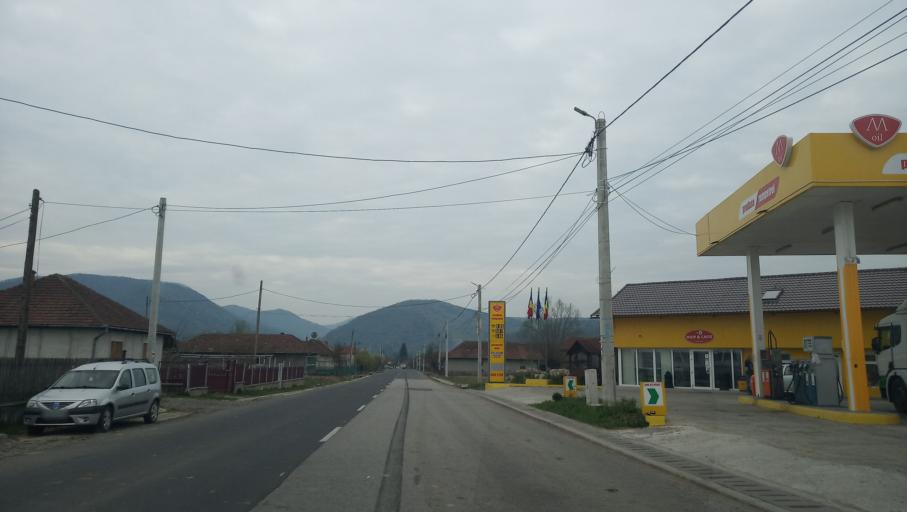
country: RO
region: Arad
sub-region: Comuna Varfurile
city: Varfurile
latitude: 46.3109
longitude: 22.5318
